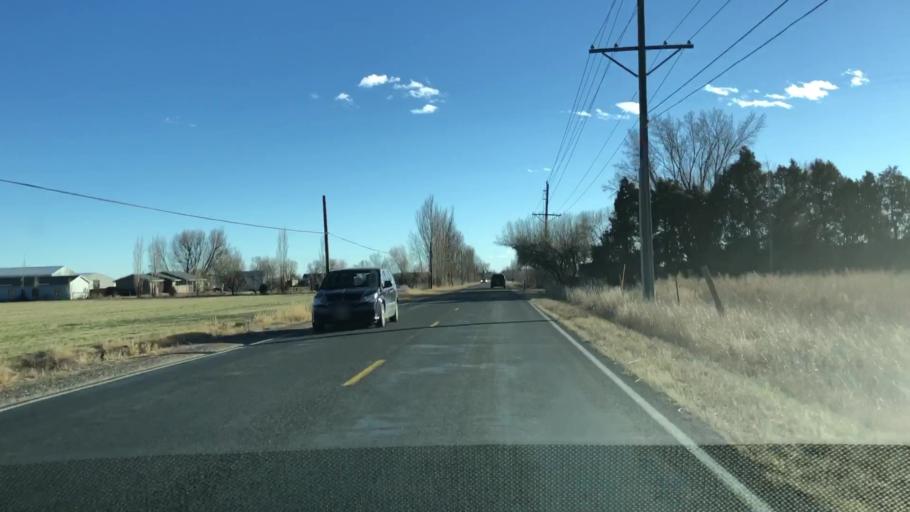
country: US
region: Colorado
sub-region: Larimer County
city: Fort Collins
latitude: 40.5499
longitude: -104.9824
